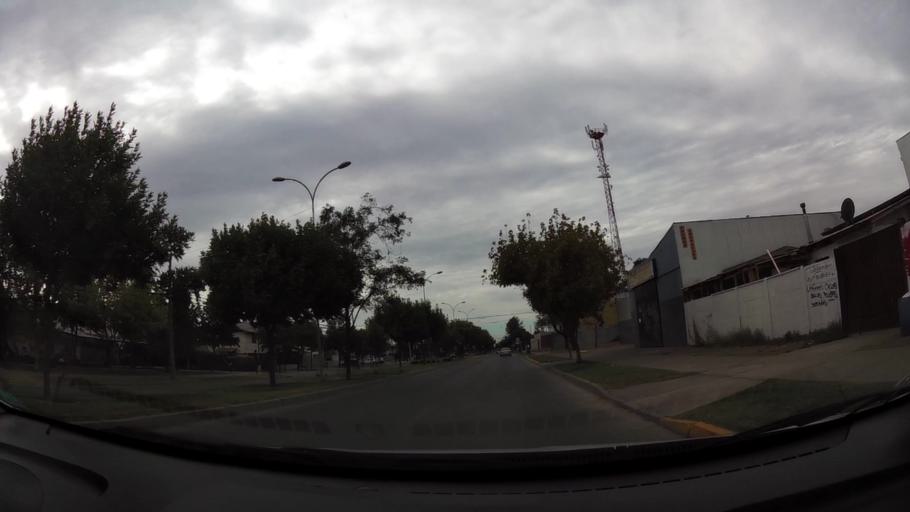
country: CL
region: O'Higgins
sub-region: Provincia de Cachapoal
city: Rancagua
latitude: -34.1619
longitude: -70.7333
